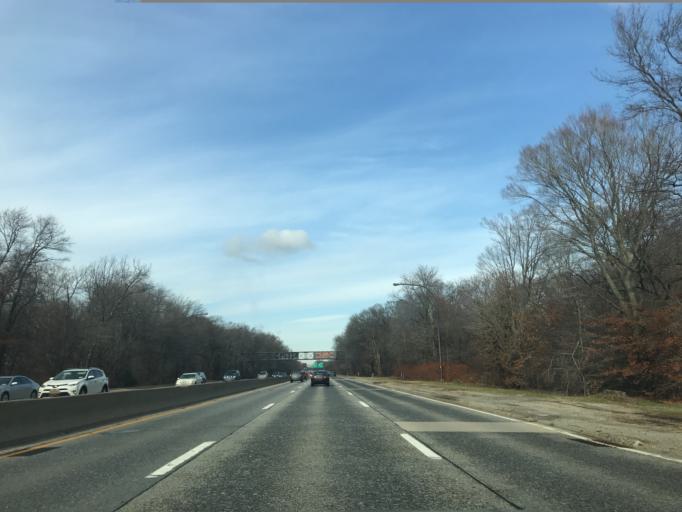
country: US
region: New York
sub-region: Nassau County
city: Uniondale
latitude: 40.7016
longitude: -73.5774
